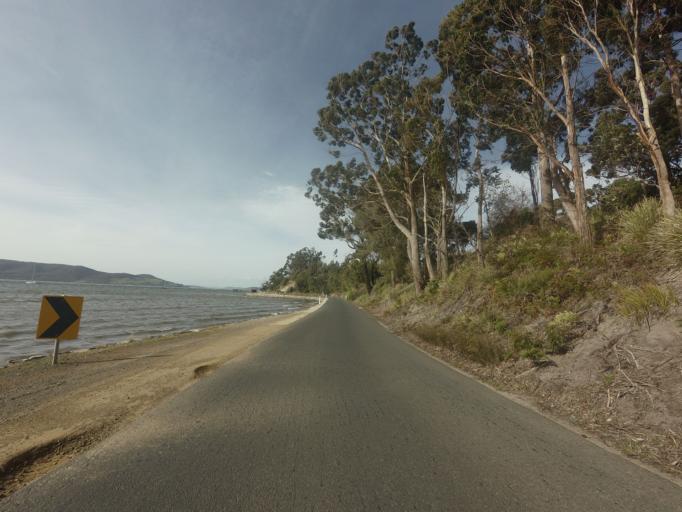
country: AU
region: Tasmania
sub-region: Kingborough
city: Margate
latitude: -43.0726
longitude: 147.2613
